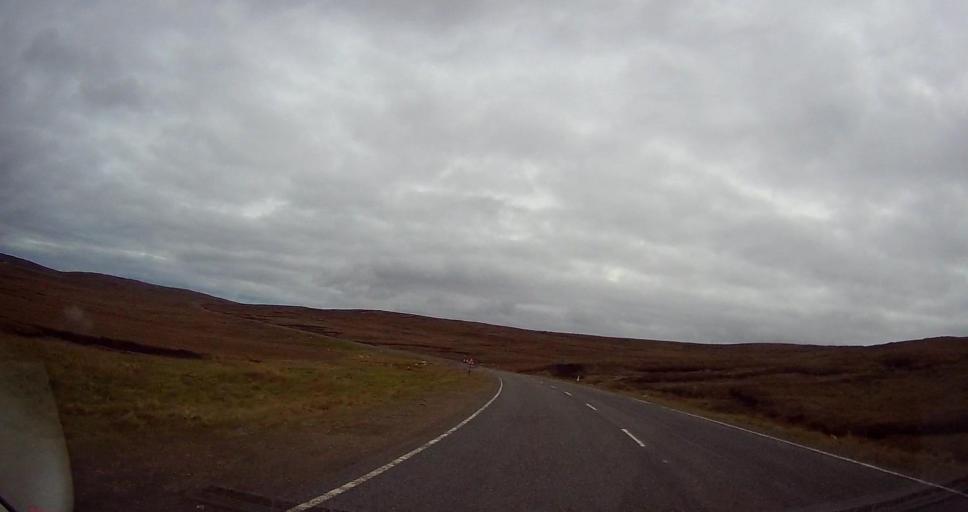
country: GB
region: Scotland
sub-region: Shetland Islands
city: Shetland
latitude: 60.6460
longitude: -1.0715
